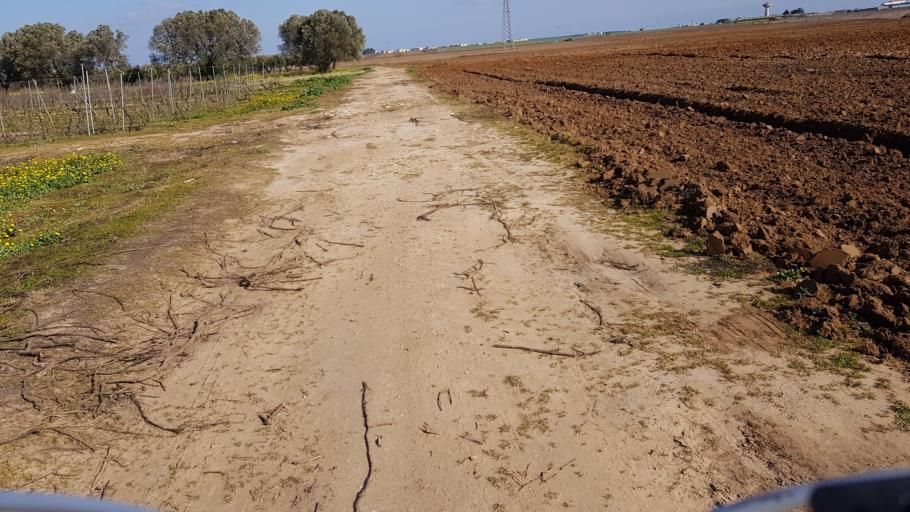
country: IT
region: Apulia
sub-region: Provincia di Brindisi
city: Brindisi
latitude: 40.6057
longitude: 17.8935
